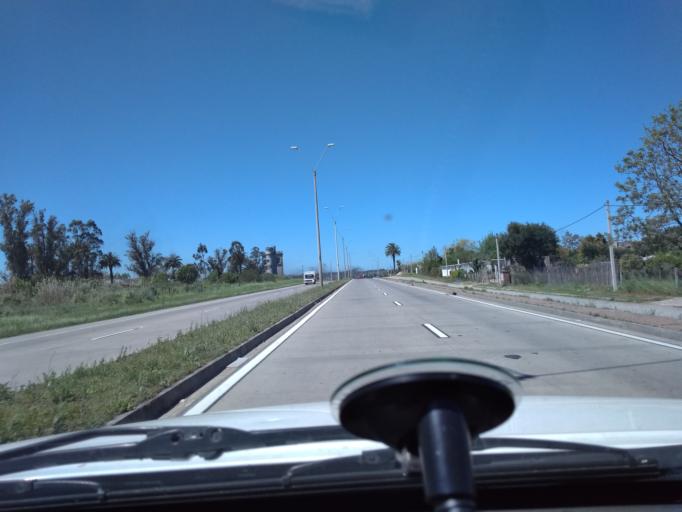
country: UY
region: Canelones
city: Toledo
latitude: -34.7949
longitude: -56.1269
